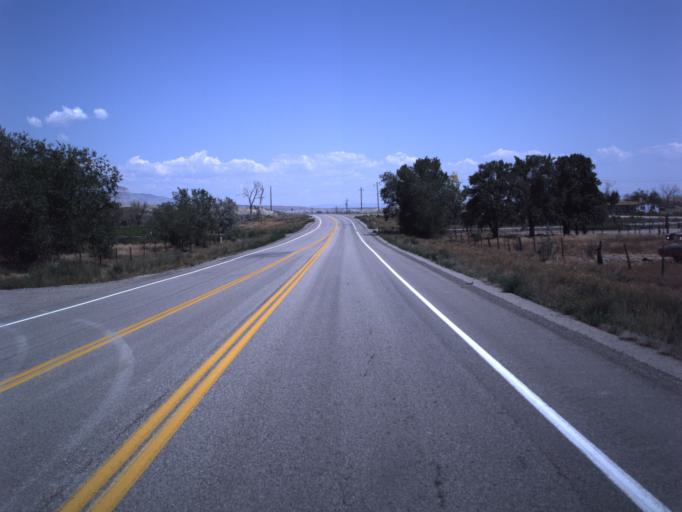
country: US
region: Utah
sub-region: Emery County
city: Ferron
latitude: 39.1353
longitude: -111.0987
